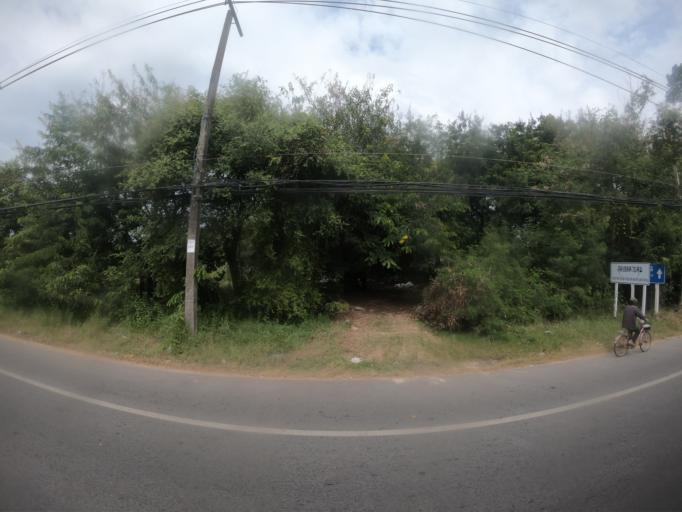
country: TH
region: Roi Et
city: Roi Et
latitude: 16.0615
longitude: 103.6245
